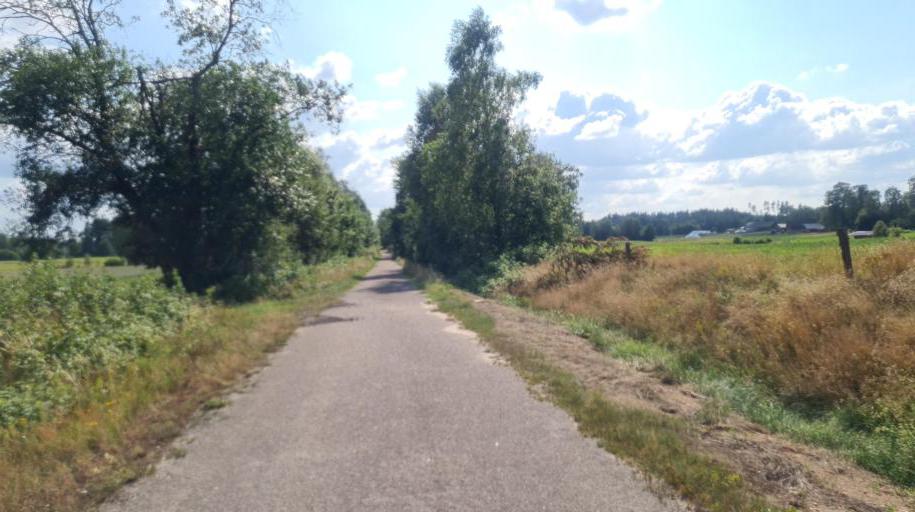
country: SE
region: Kronoberg
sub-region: Ljungby Kommun
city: Ljungby
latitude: 56.7971
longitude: 13.9105
